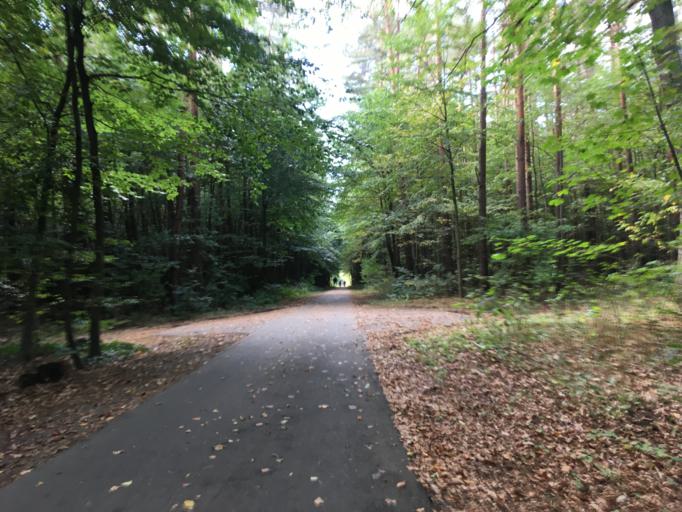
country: DE
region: Brandenburg
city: Petershagen
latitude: 52.5538
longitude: 13.8042
